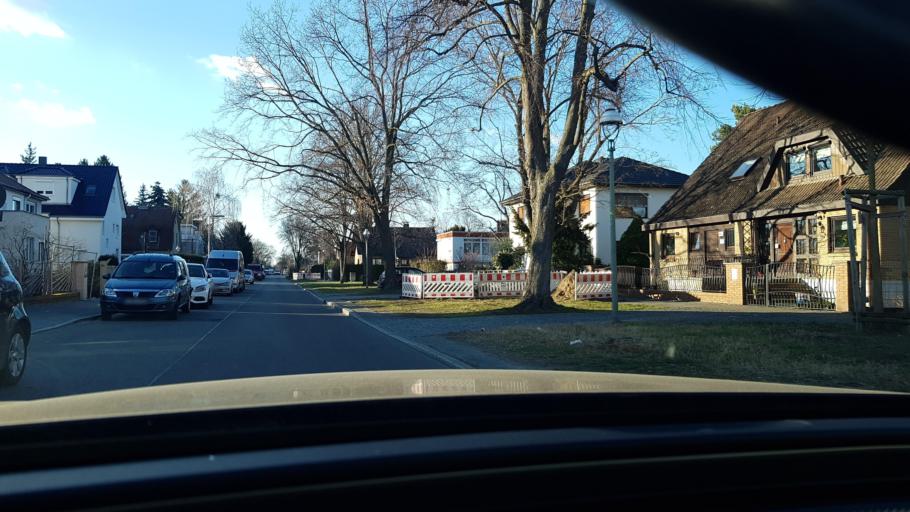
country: DE
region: Berlin
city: Rudow
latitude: 52.4288
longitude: 13.4886
